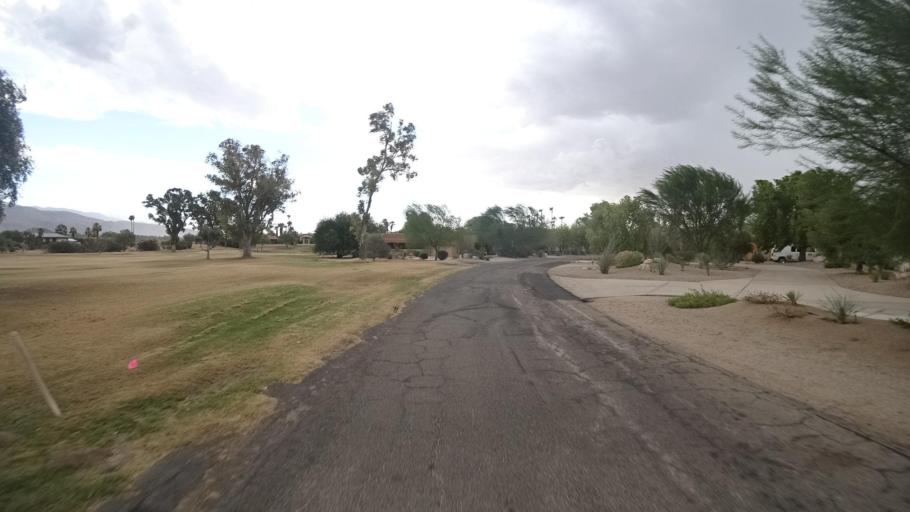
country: US
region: California
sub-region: San Diego County
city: Borrego Springs
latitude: 33.2953
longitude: -116.3885
